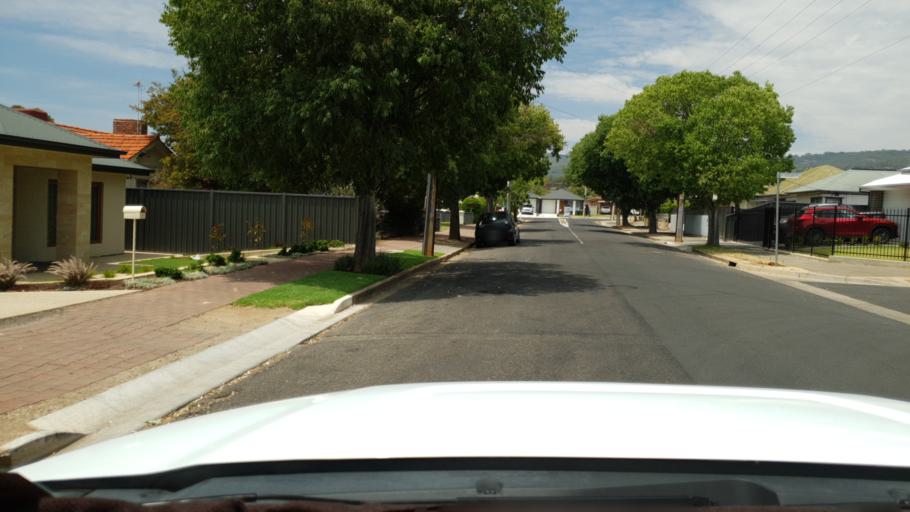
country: AU
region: South Australia
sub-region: Marion
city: Clovelly Park
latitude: -35.0006
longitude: 138.5799
